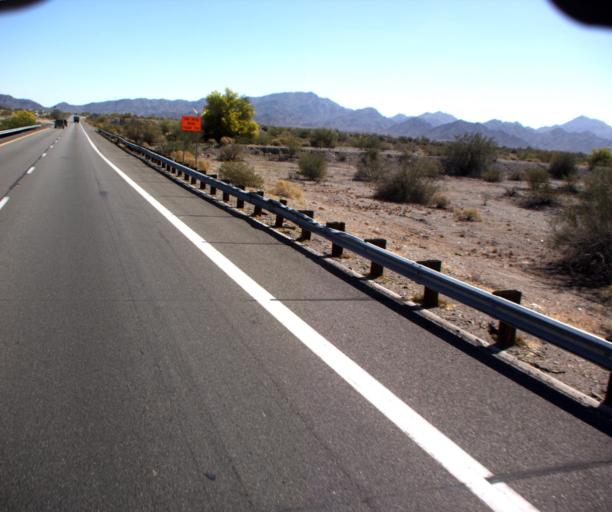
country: US
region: Arizona
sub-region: La Paz County
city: Ehrenberg
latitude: 33.6158
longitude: -114.4629
